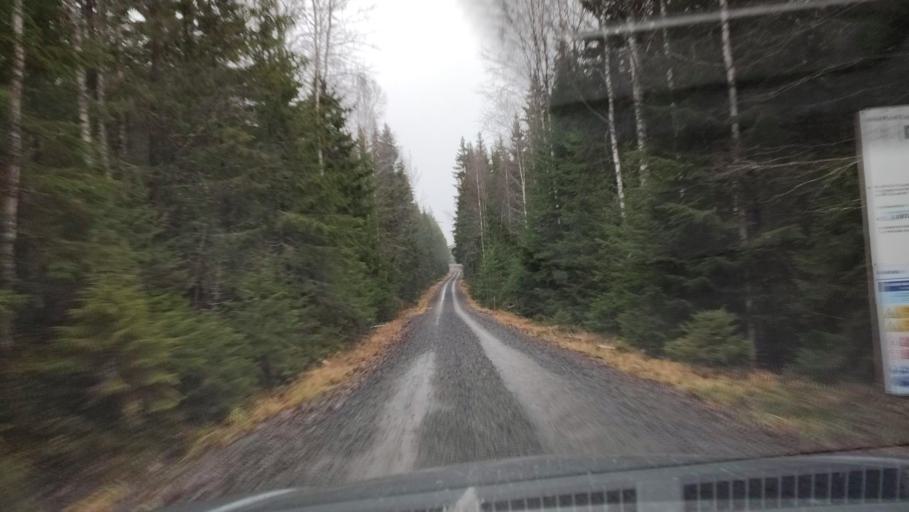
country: FI
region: Southern Ostrobothnia
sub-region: Suupohja
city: Karijoki
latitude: 62.1405
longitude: 21.6274
